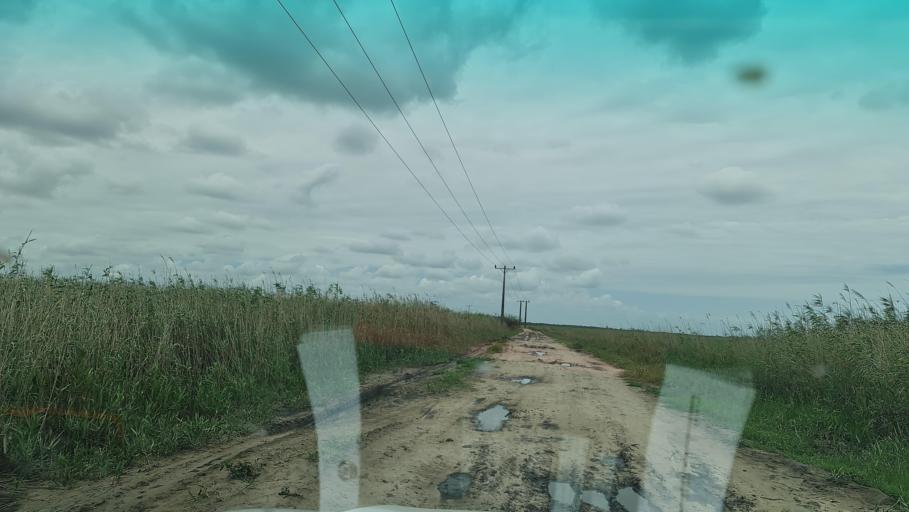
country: MZ
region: Maputo City
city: Maputo
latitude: -25.7171
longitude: 32.7014
